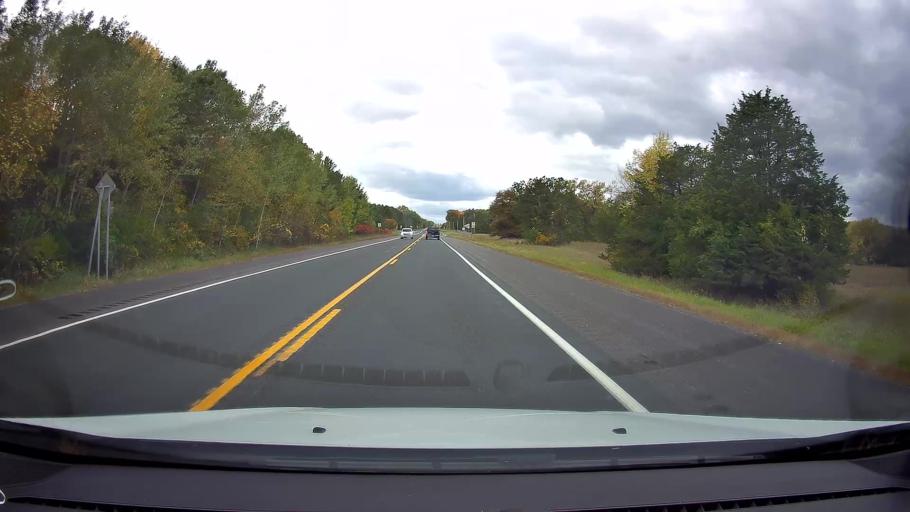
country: US
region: Wisconsin
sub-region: Polk County
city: Saint Croix Falls
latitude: 45.4190
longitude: -92.6588
